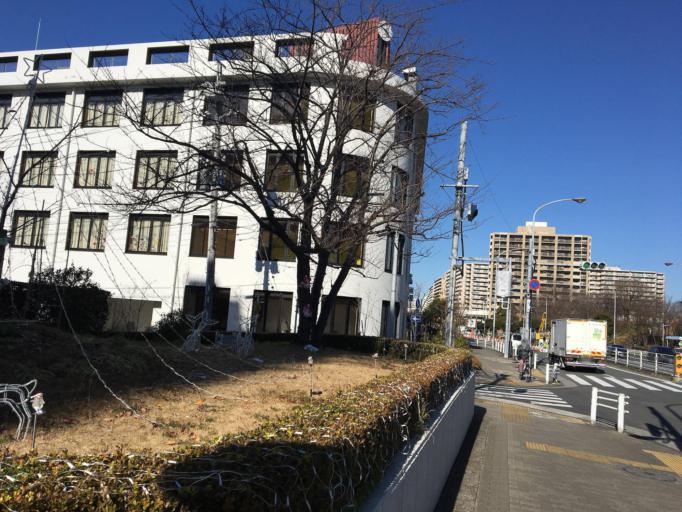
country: JP
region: Tokyo
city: Urayasu
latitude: 35.6876
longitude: 139.8451
